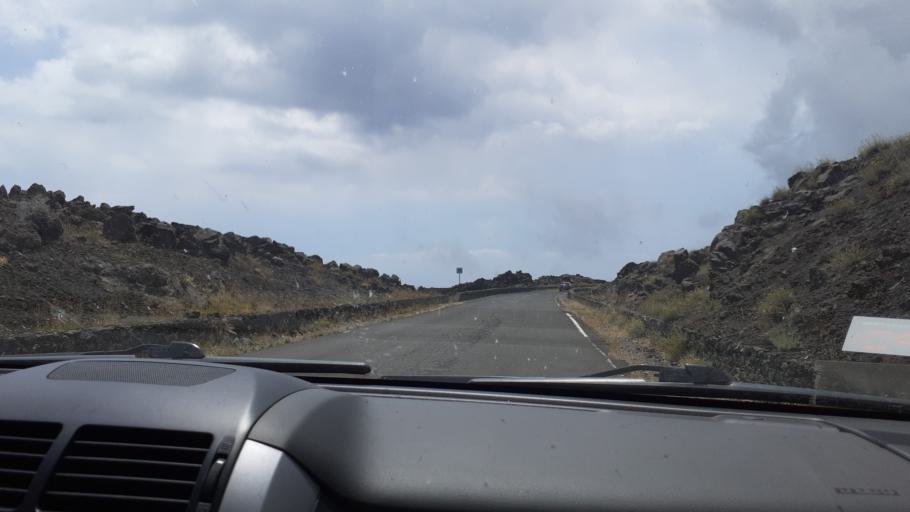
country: IT
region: Sicily
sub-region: Catania
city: Nicolosi
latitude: 37.6900
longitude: 15.0200
